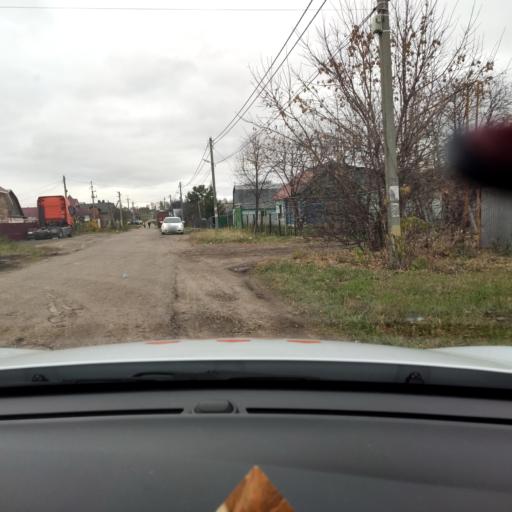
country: RU
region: Tatarstan
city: Vysokaya Gora
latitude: 55.8739
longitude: 49.2524
